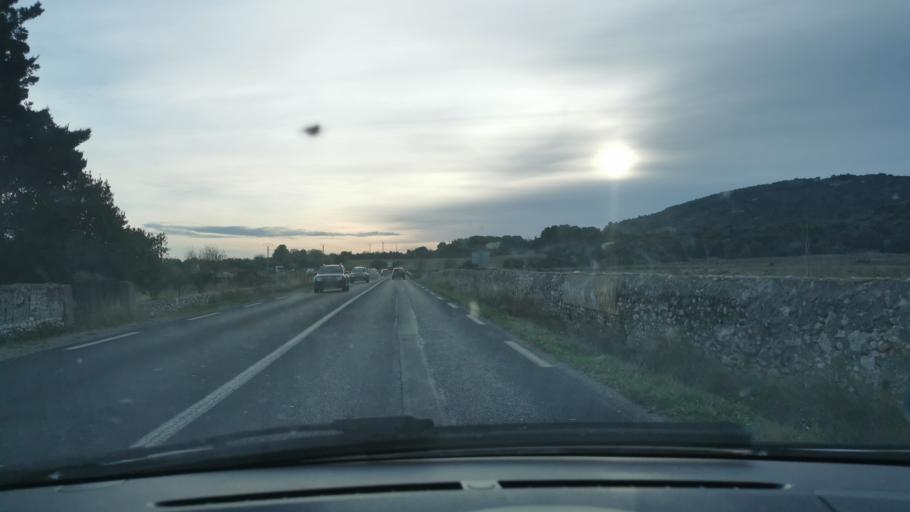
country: FR
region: Languedoc-Roussillon
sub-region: Departement de l'Herault
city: Frontignan
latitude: 43.4703
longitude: 3.7674
